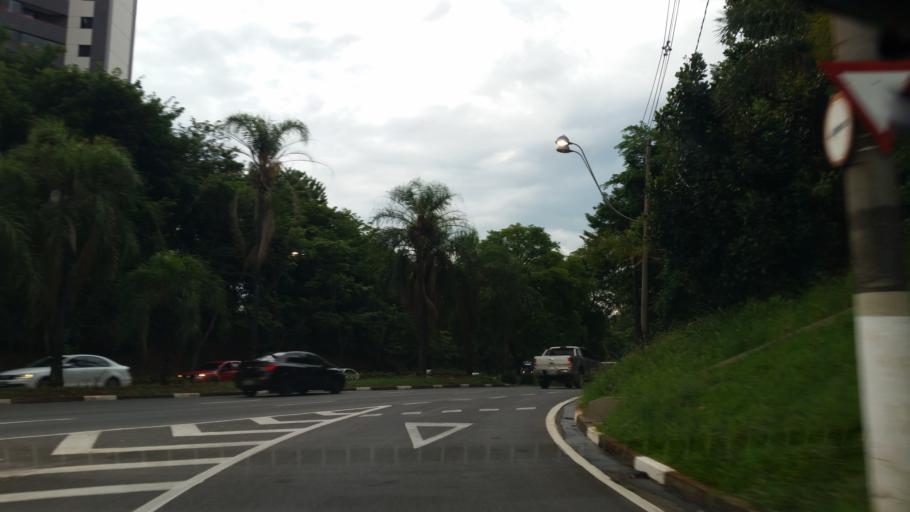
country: BR
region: Sao Paulo
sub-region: Campinas
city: Campinas
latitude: -22.9177
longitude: -47.0615
